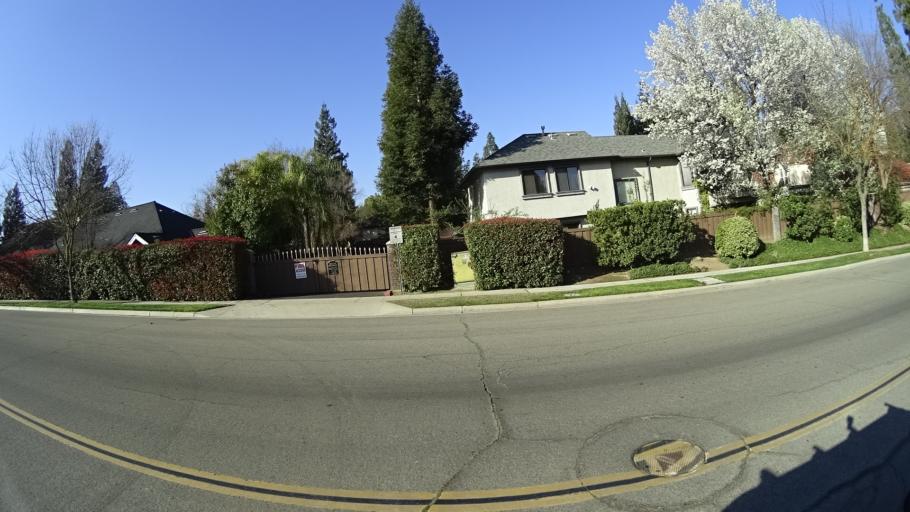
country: US
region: California
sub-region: Fresno County
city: Clovis
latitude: 36.8607
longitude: -119.7958
